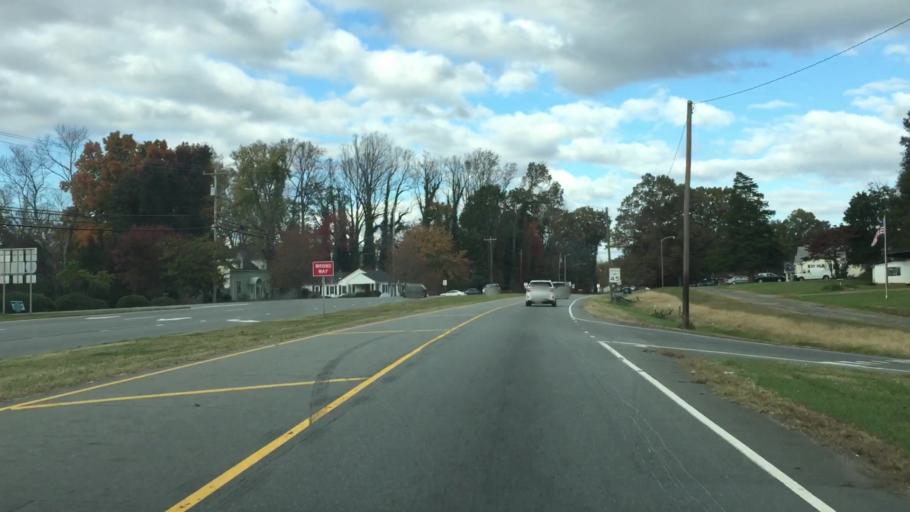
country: US
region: North Carolina
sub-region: Forsyth County
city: Winston-Salem
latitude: 36.1151
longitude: -80.1870
